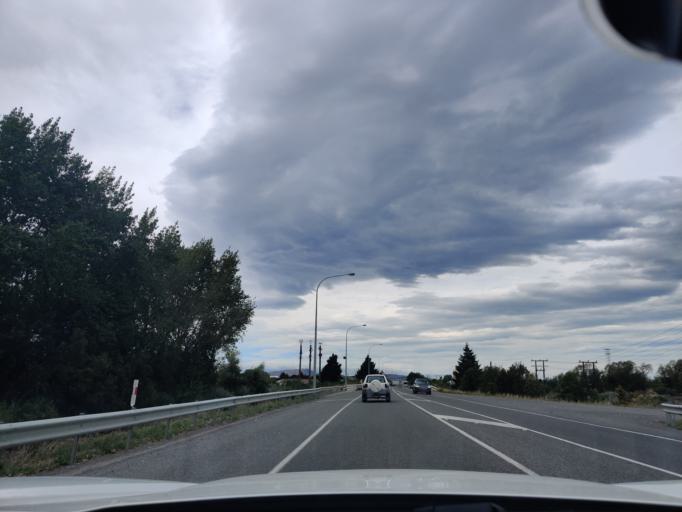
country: NZ
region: Wellington
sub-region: Masterton District
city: Masterton
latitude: -40.9658
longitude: 175.6074
